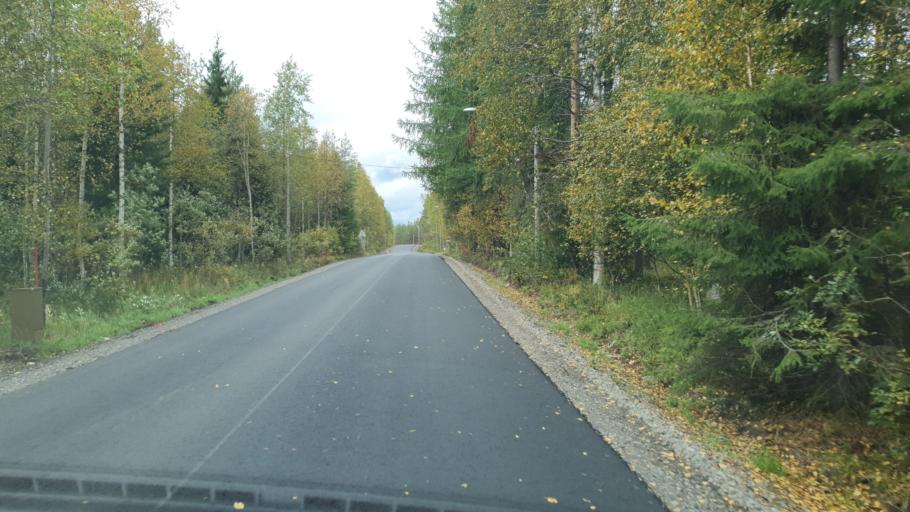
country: FI
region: Lapland
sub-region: Rovaniemi
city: Rovaniemi
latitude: 66.4219
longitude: 25.4049
